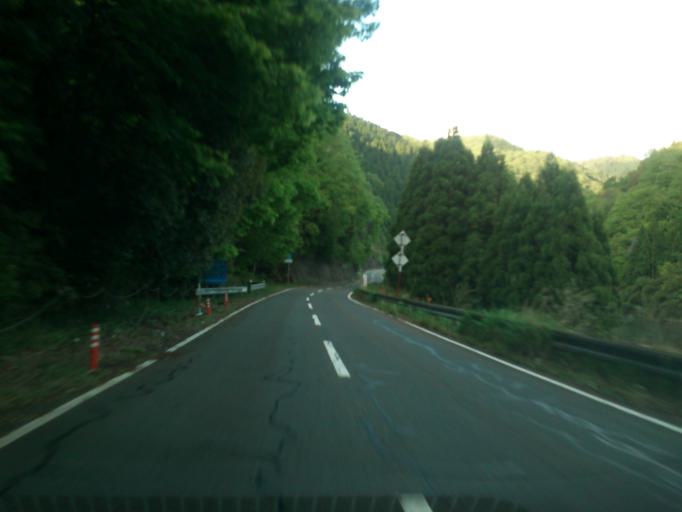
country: JP
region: Kyoto
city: Ayabe
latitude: 35.2749
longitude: 135.3533
